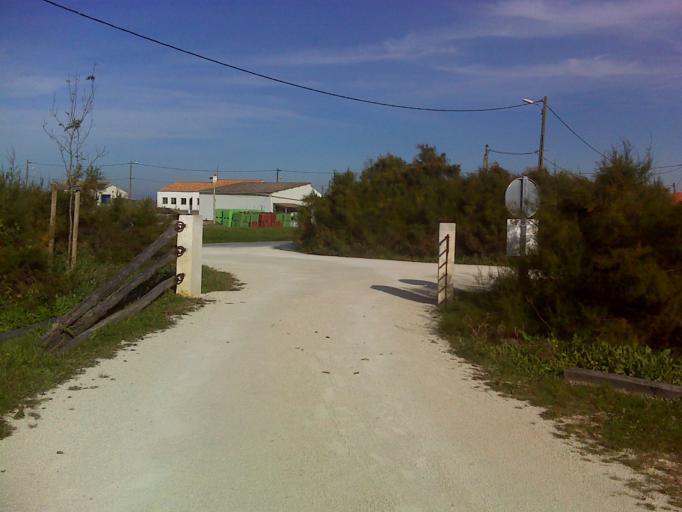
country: FR
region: Poitou-Charentes
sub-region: Departement de la Charente-Maritime
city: Marennes
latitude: 45.8687
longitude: -1.0690
